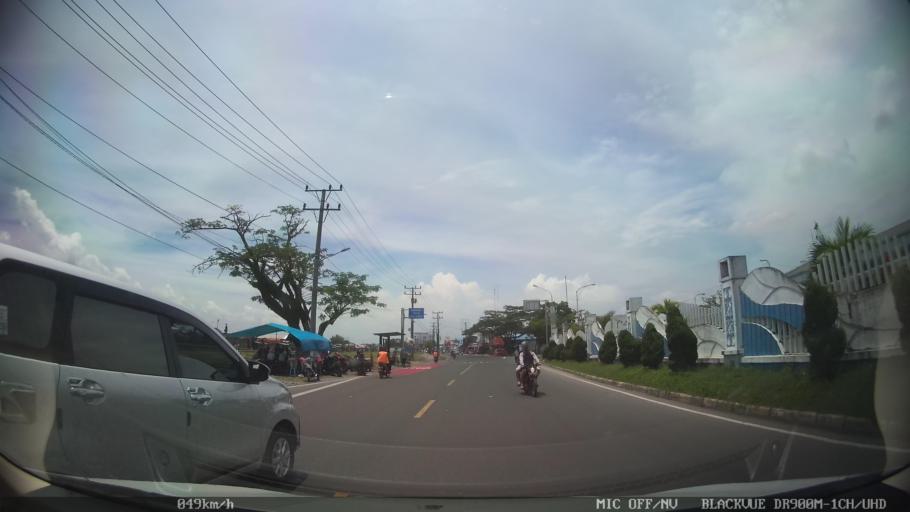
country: ID
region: North Sumatra
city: Belawan
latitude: 3.7783
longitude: 98.6814
